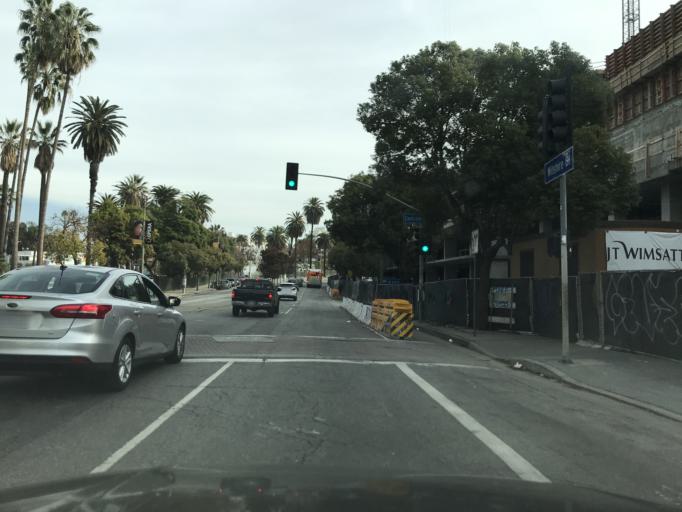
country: US
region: California
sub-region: Los Angeles County
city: Silver Lake
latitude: 34.0618
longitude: -118.2860
